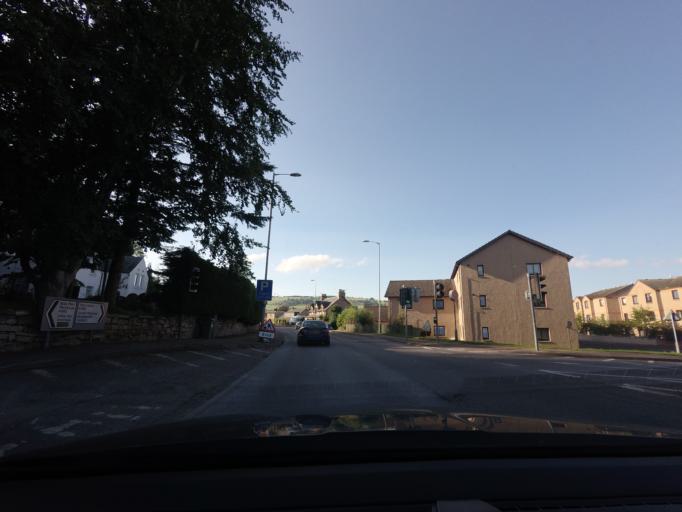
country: GB
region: Scotland
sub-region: Highland
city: Dingwall
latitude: 57.5923
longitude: -4.4240
